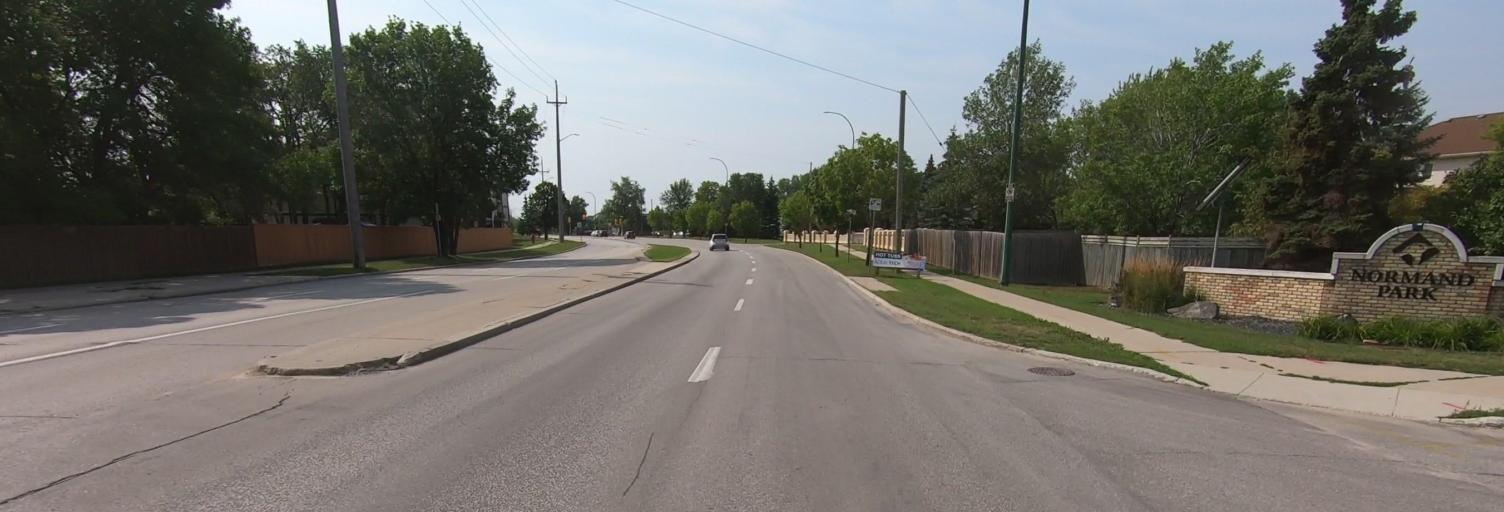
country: CA
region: Manitoba
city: Winnipeg
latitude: 49.8035
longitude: -97.1158
